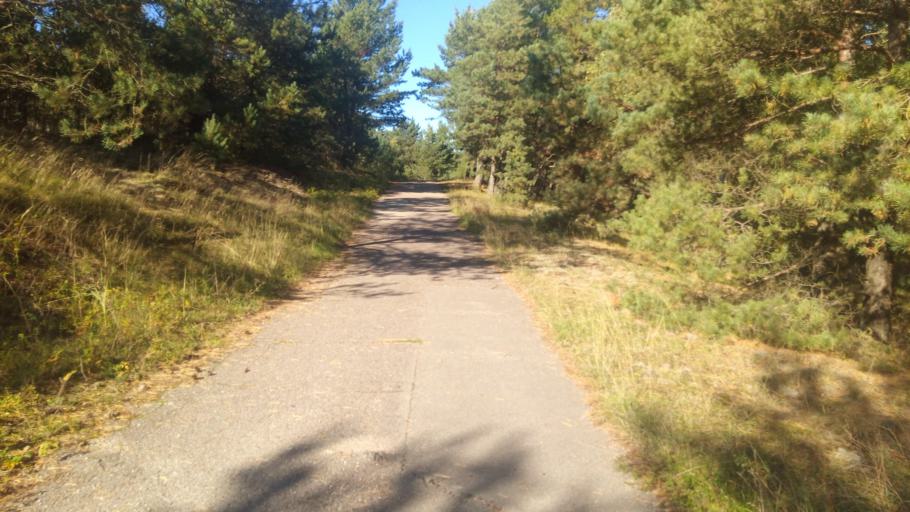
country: LT
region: Klaipedos apskritis
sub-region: Klaipeda
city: Klaipeda
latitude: 55.7121
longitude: 21.0998
